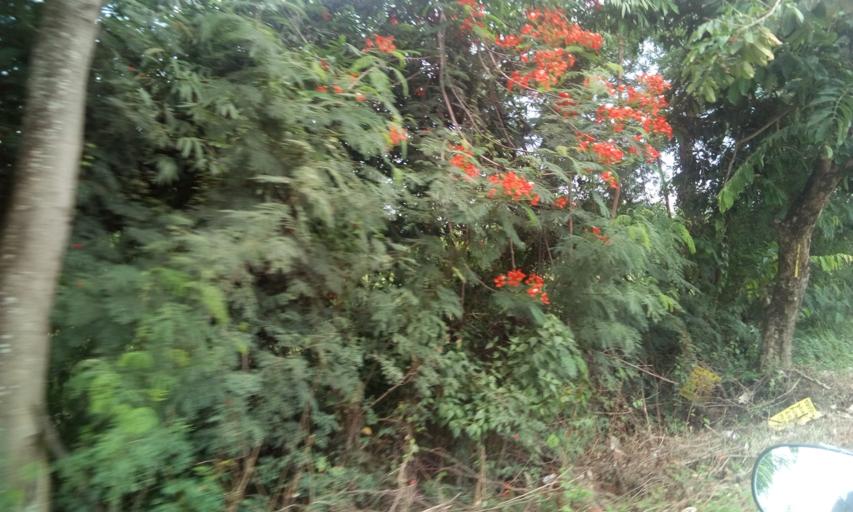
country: TH
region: Pathum Thani
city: Ban Lam Luk Ka
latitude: 14.0034
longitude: 100.8423
